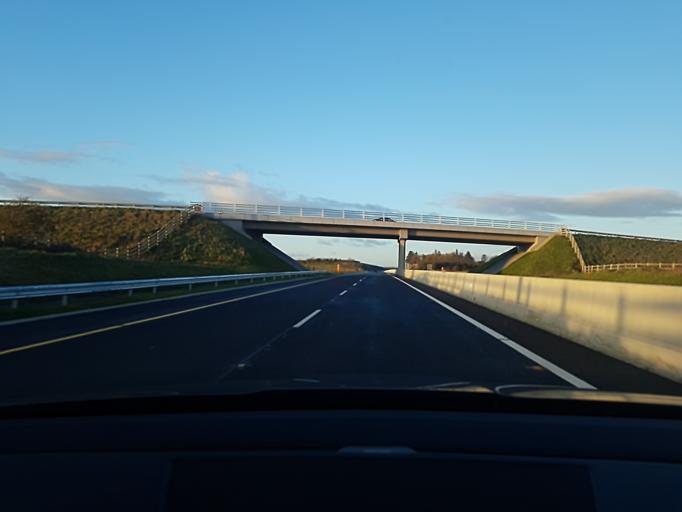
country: IE
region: Connaught
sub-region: County Galway
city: Athenry
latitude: 53.3377
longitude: -8.8021
